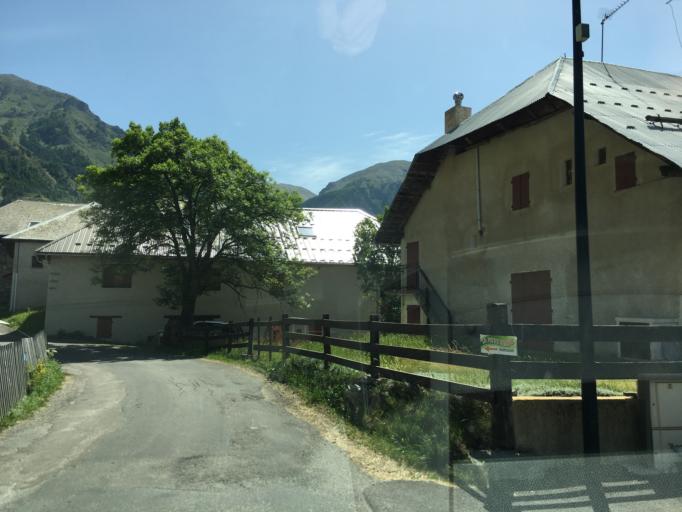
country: FR
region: Provence-Alpes-Cote d'Azur
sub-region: Departement des Hautes-Alpes
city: Guillestre
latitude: 44.5478
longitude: 6.6195
